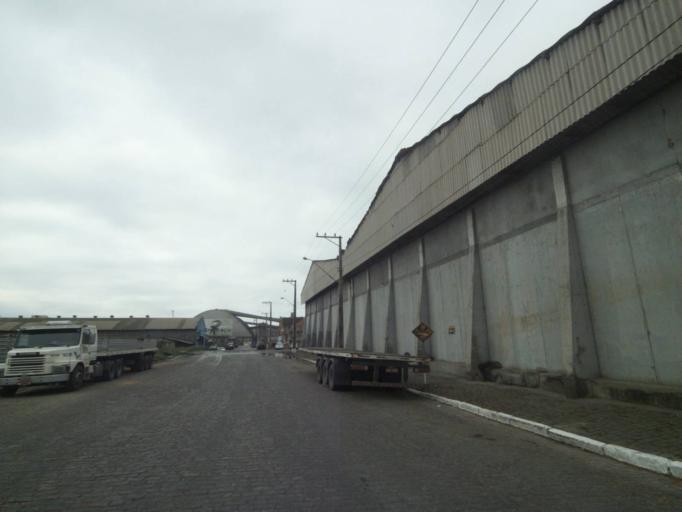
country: BR
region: Parana
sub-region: Paranagua
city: Paranagua
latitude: -25.5103
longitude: -48.5149
